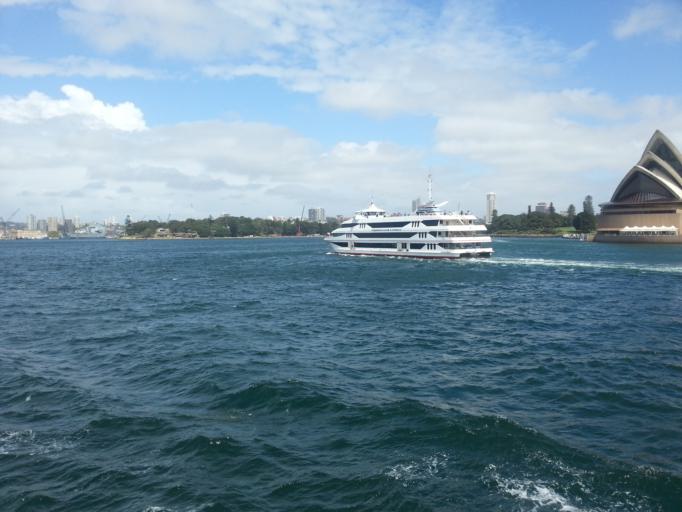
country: AU
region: New South Wales
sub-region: North Sydney
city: Kirribilli
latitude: -33.8537
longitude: 151.2161
